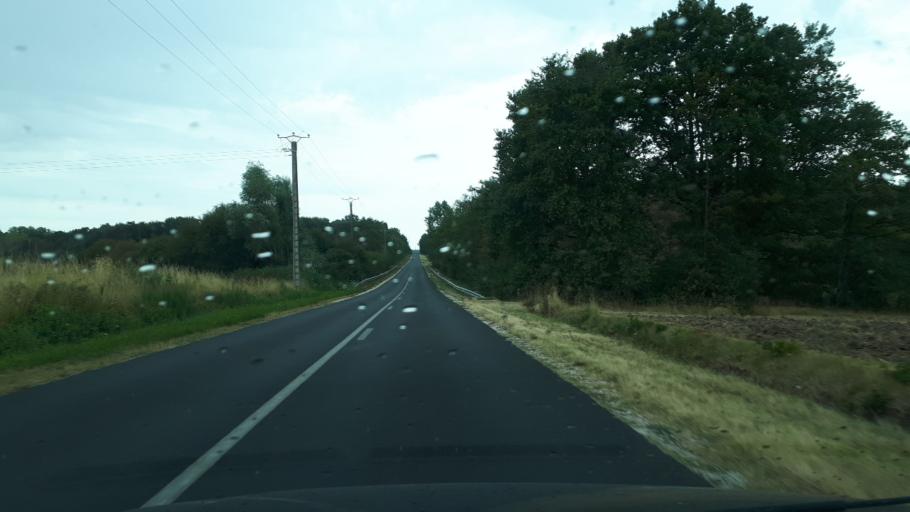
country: FR
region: Centre
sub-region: Departement du Loir-et-Cher
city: Saint-Romain-sur-Cher
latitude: 47.3503
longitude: 1.4029
